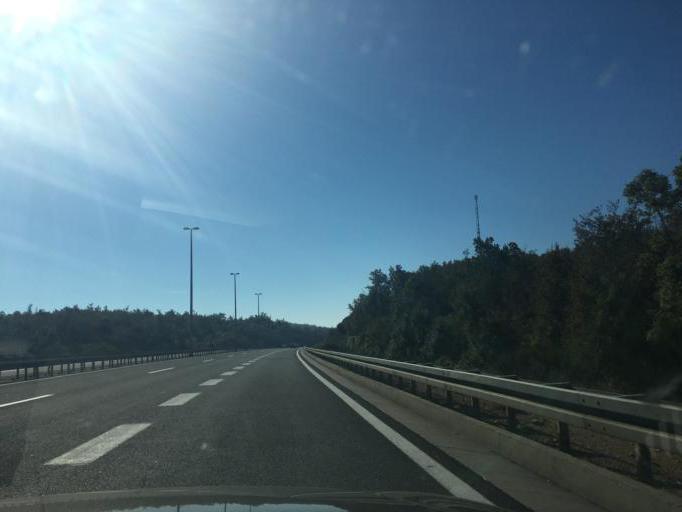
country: HR
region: Licko-Senjska
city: Otocac
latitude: 44.7498
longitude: 15.3752
